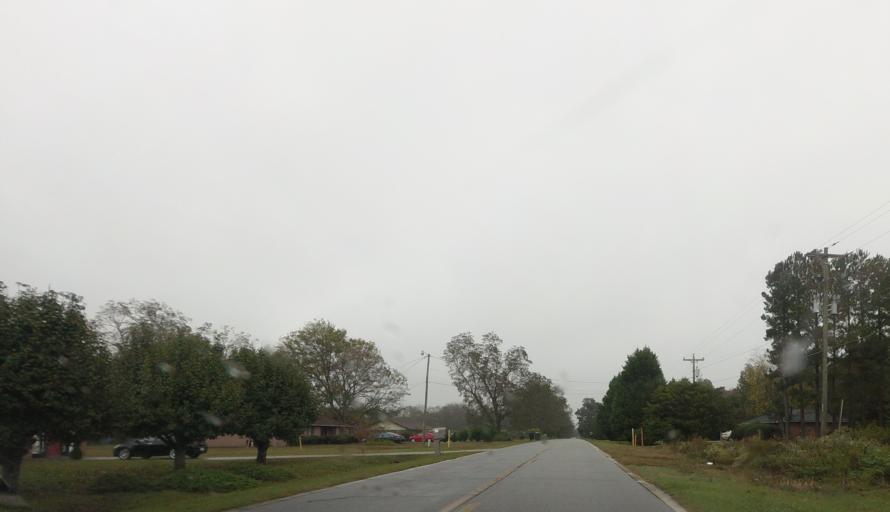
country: US
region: Georgia
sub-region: Peach County
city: Fort Valley
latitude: 32.5461
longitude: -83.9141
